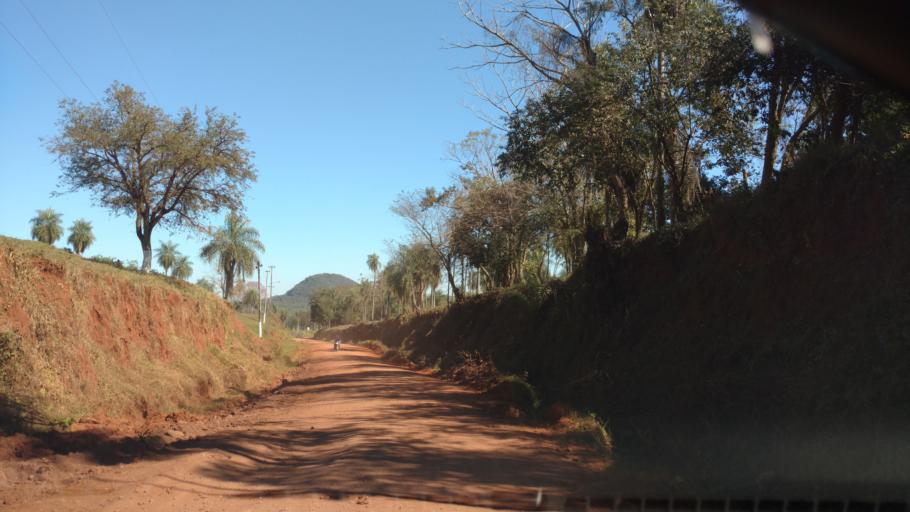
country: PY
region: Paraguari
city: Yaguaron
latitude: -25.5643
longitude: -57.3039
